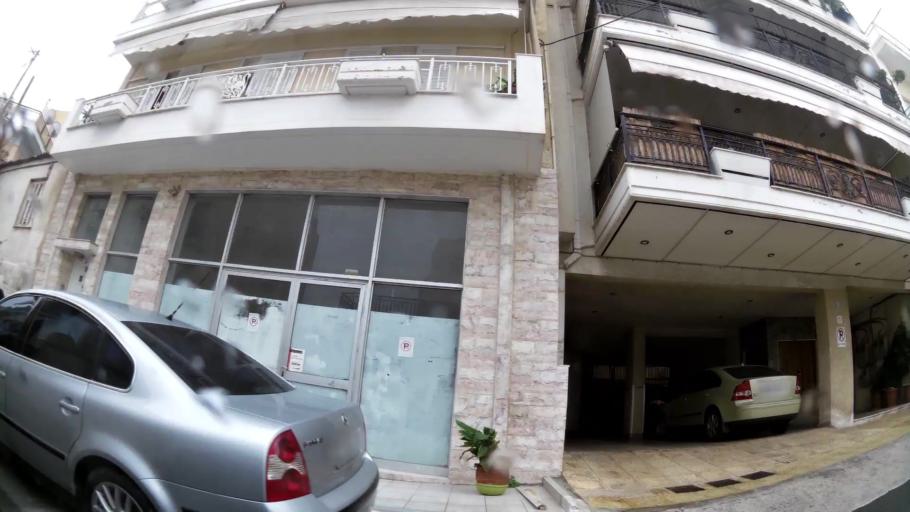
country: GR
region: Attica
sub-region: Nomos Piraios
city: Nikaia
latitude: 37.9574
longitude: 23.6476
